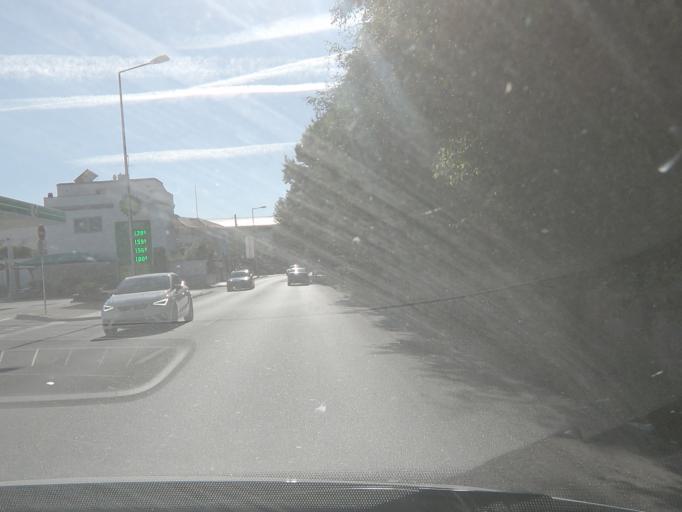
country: PT
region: Viseu
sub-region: Viseu
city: Viseu
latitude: 40.6557
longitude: -7.9022
